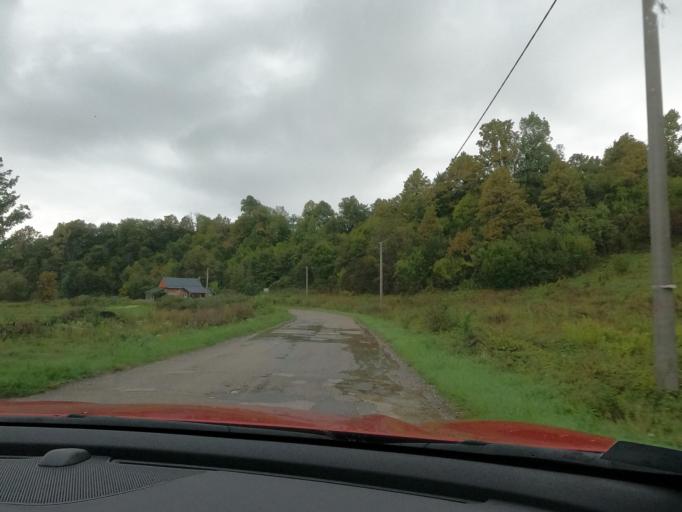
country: HR
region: Sisacko-Moslavacka
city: Glina
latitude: 45.2964
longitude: 16.1487
